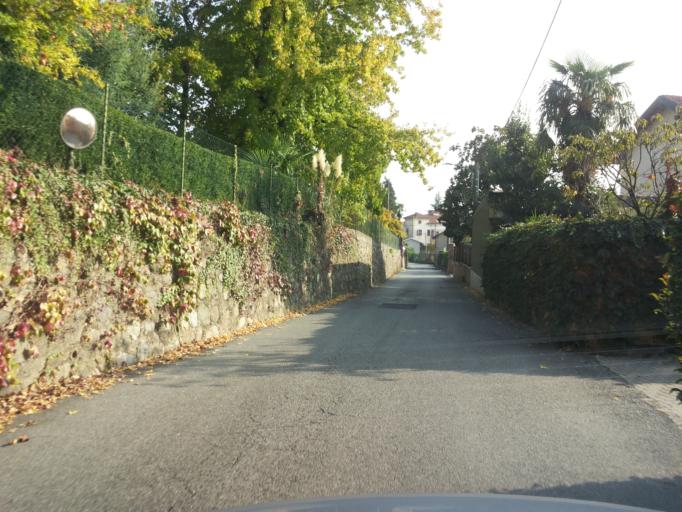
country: IT
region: Piedmont
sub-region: Provincia di Biella
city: Viverone
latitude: 45.4293
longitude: 8.0467
